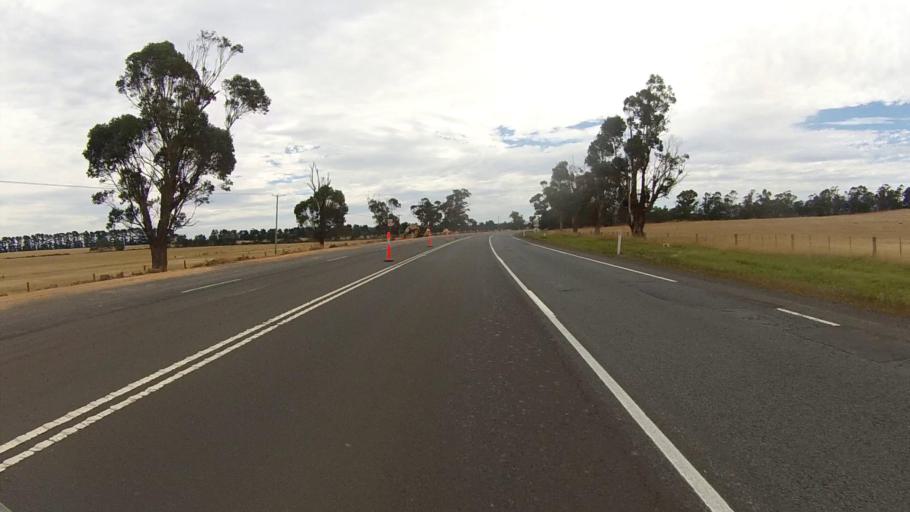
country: AU
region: Tasmania
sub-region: Northern Midlands
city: Evandale
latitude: -41.6247
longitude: 147.2260
